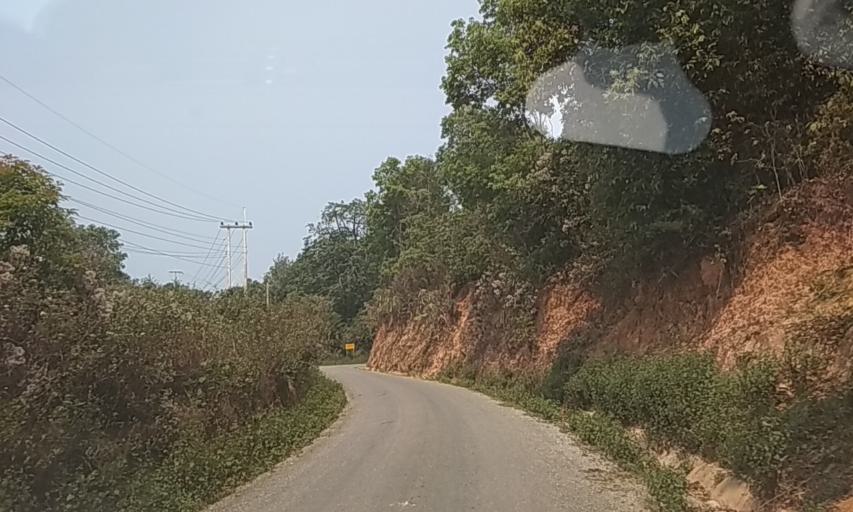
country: TH
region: Nan
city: Chaloem Phra Kiat
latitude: 20.0164
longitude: 101.1146
